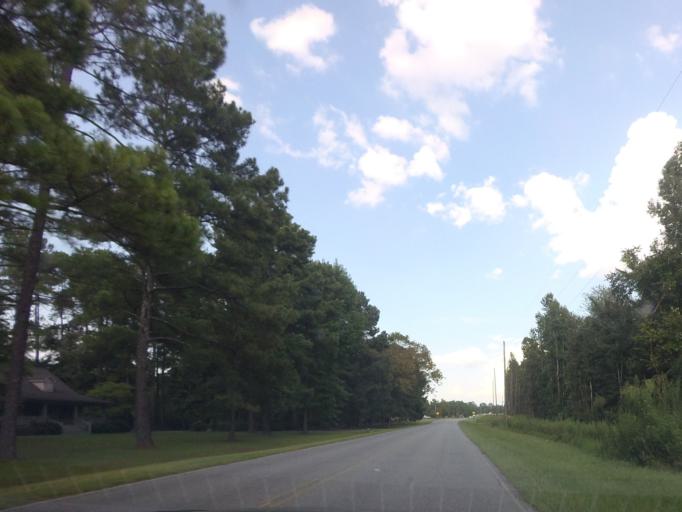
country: US
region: Georgia
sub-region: Bleckley County
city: Cochran
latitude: 32.3838
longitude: -83.3311
